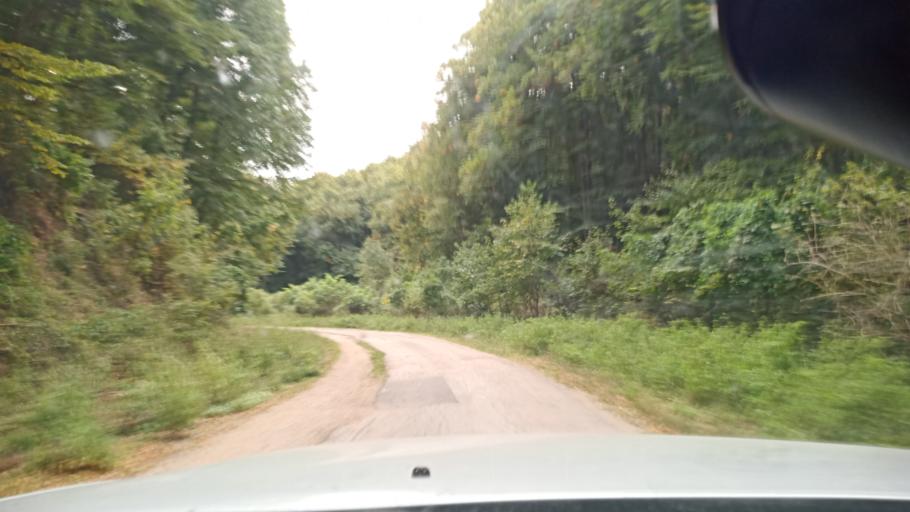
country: HU
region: Komarom-Esztergom
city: Oroszlany
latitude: 47.3945
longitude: 18.3134
